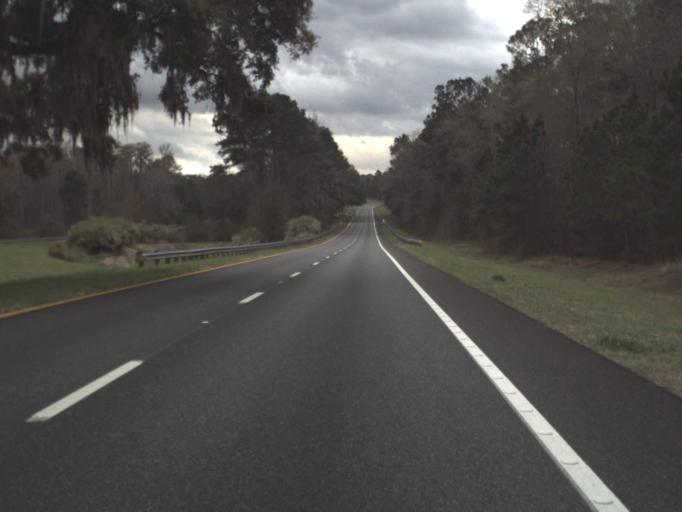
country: US
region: Georgia
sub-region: Grady County
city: Cairo
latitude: 30.6525
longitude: -84.1692
